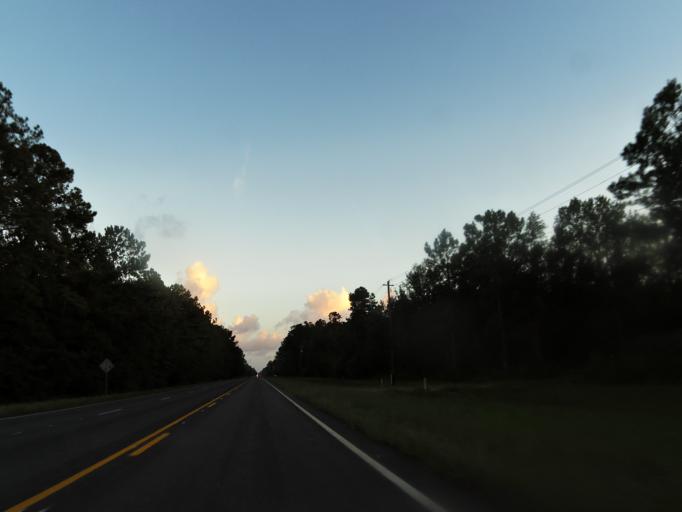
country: US
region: Georgia
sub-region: Camden County
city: Kingsland
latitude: 30.8533
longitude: -81.7010
